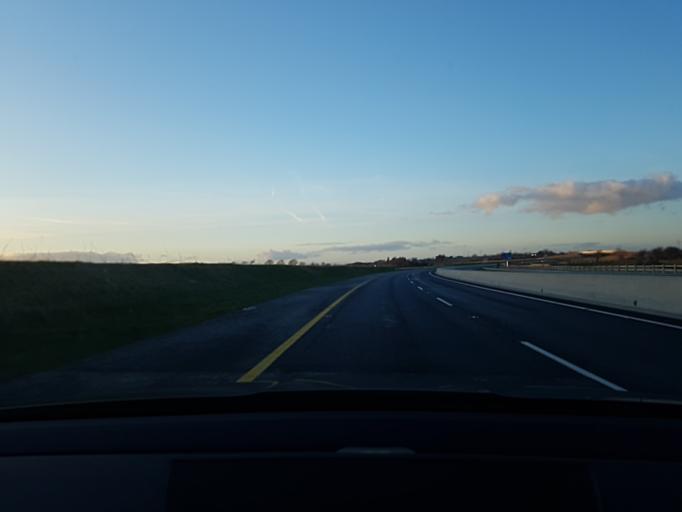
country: IE
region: Connaught
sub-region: County Galway
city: Tuam
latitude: 53.4930
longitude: -8.8738
